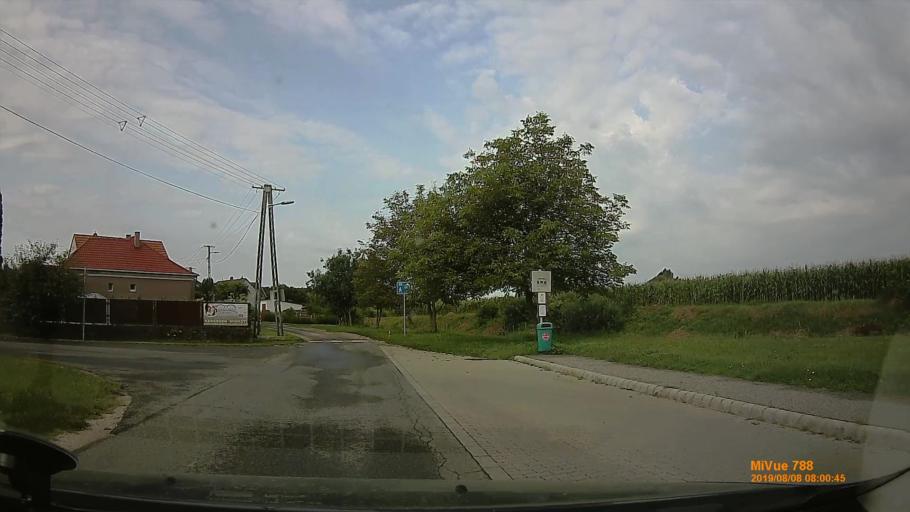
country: HU
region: Zala
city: Nagykanizsa
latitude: 46.4624
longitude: 16.9580
